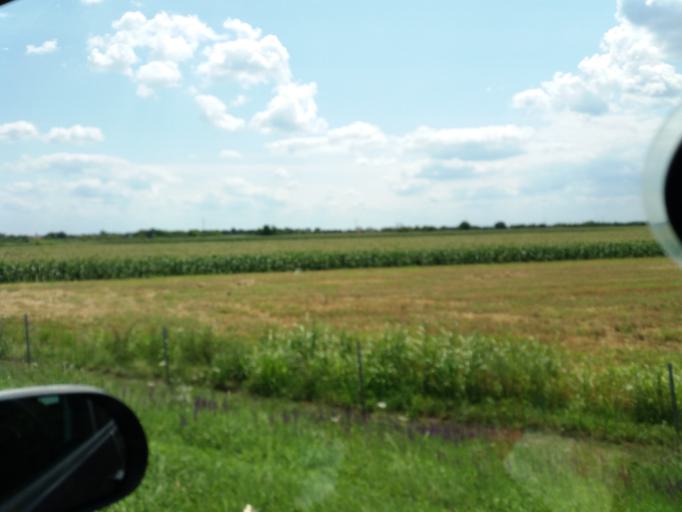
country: RS
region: Autonomna Pokrajina Vojvodina
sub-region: Sremski Okrug
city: Pecinci
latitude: 44.9181
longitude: 19.9553
